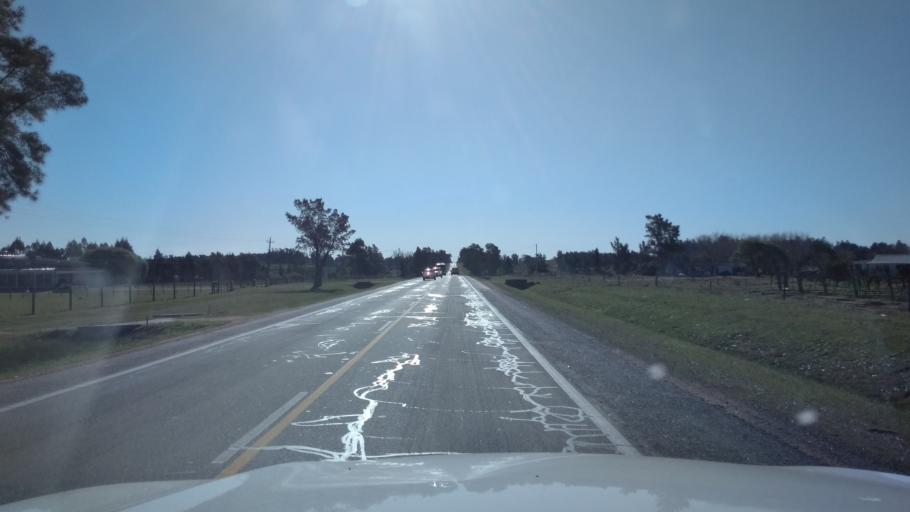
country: UY
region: Canelones
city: San Jacinto
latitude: -34.5970
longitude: -55.8307
